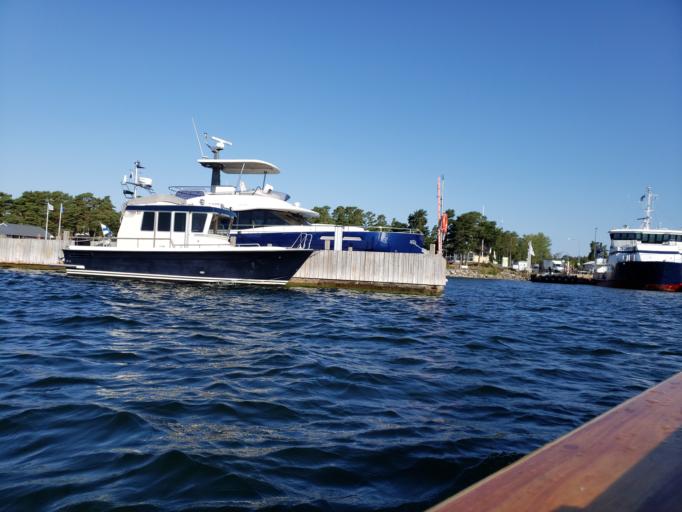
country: FI
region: Varsinais-Suomi
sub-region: Aboland-Turunmaa
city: Dragsfjaerd
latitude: 59.9203
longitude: 22.4113
